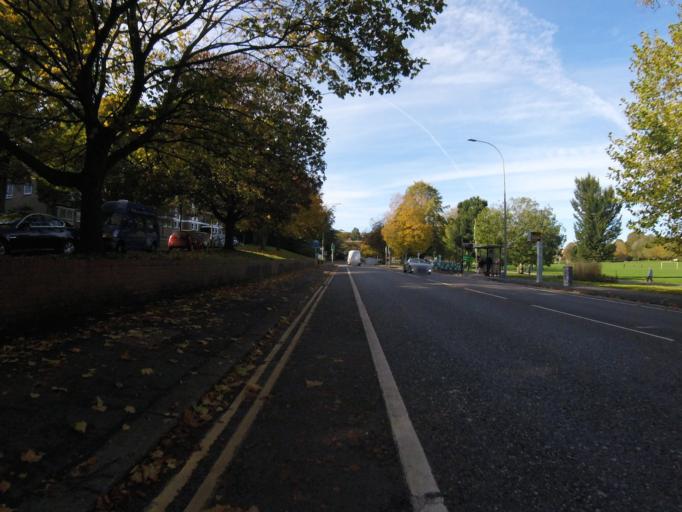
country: GB
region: England
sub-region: Brighton and Hove
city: Brighton
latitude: 50.8387
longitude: -0.1477
